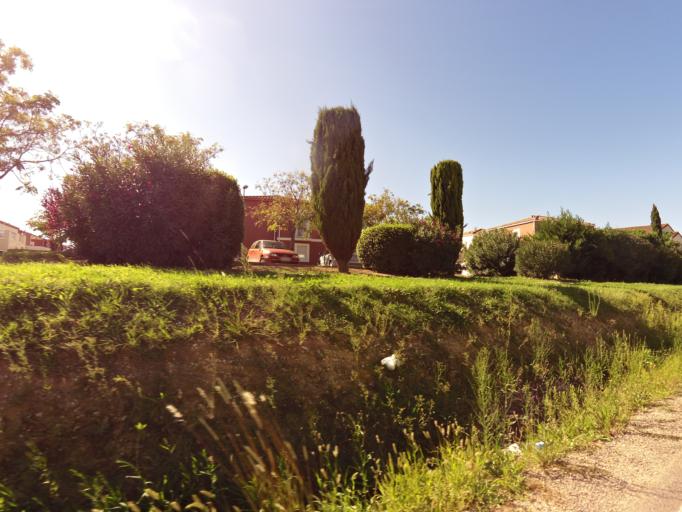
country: FR
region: Languedoc-Roussillon
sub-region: Departement de l'Herault
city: Lunel
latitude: 43.6654
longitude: 4.1337
